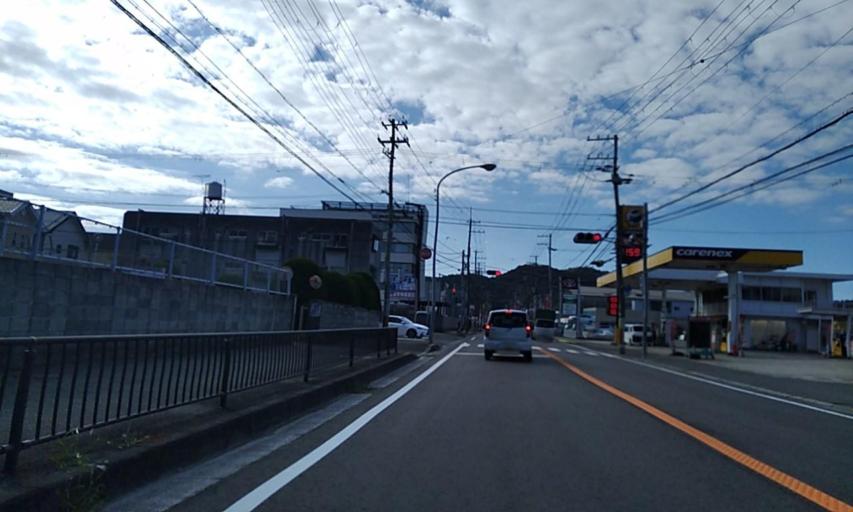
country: JP
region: Wakayama
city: Minato
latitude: 34.2007
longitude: 135.1591
